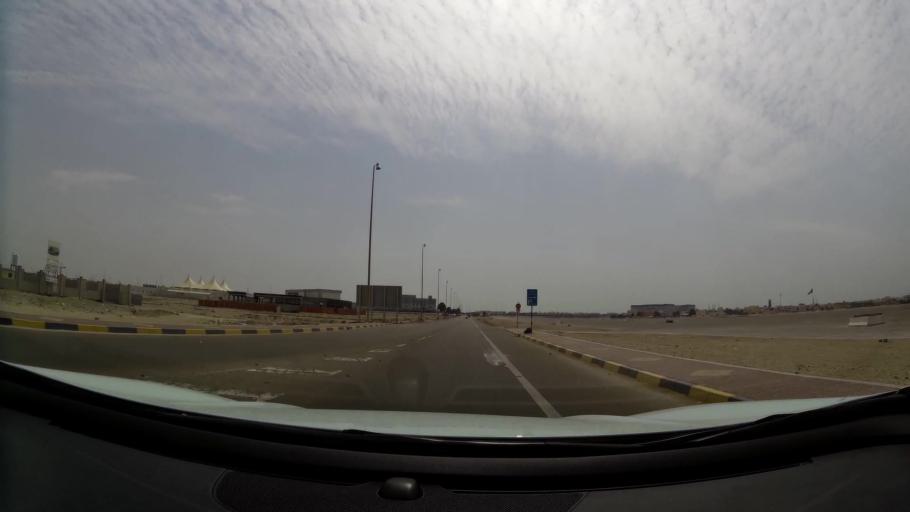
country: AE
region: Abu Dhabi
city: Abu Dhabi
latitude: 24.5378
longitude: 54.6761
